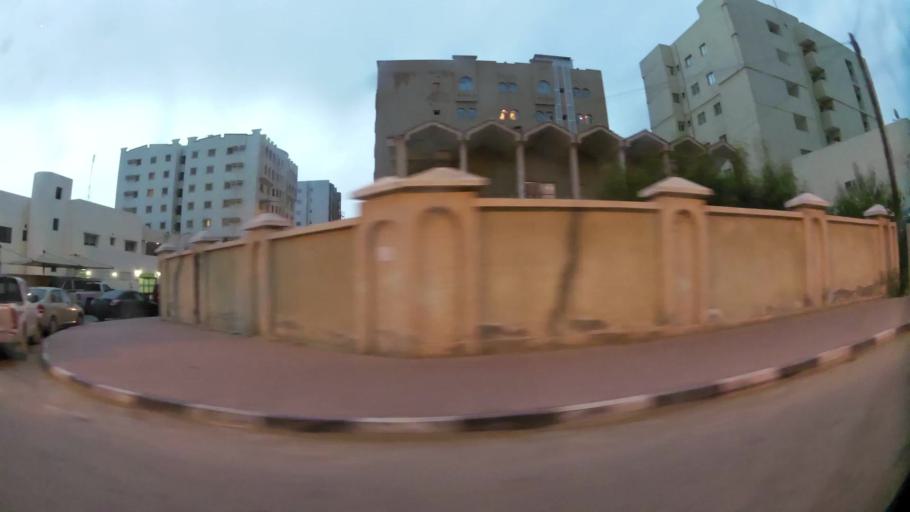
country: QA
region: Baladiyat ad Dawhah
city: Doha
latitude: 25.2713
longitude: 51.5210
